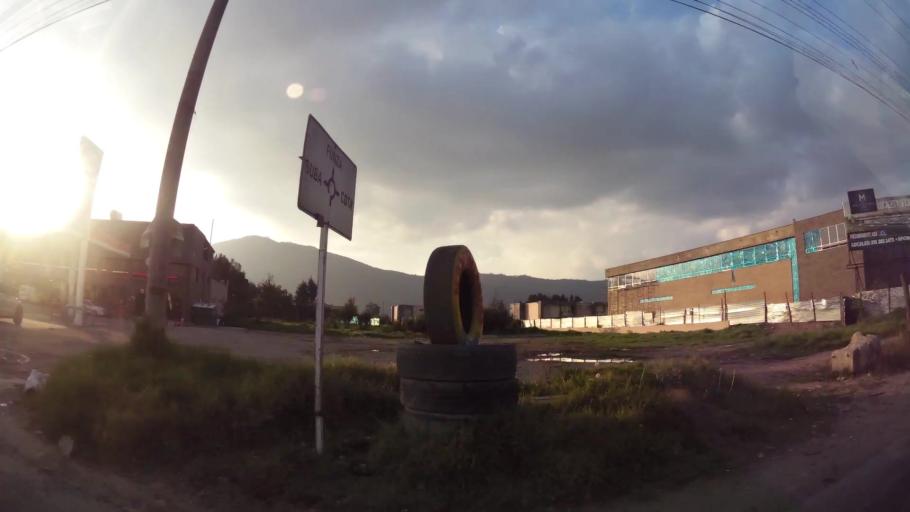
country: CO
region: Cundinamarca
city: Cota
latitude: 4.8025
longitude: -74.0963
